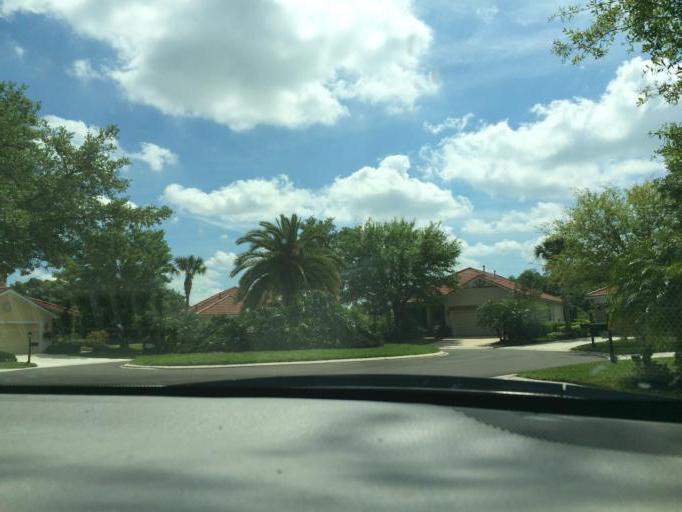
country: US
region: Florida
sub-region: Manatee County
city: Ellenton
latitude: 27.5094
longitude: -82.4445
